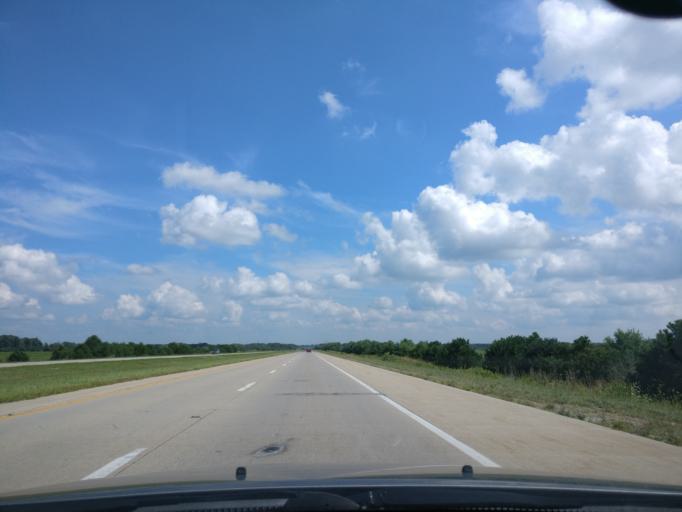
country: US
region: Ohio
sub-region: Greene County
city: Wilberforce
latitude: 39.6821
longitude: -83.8347
